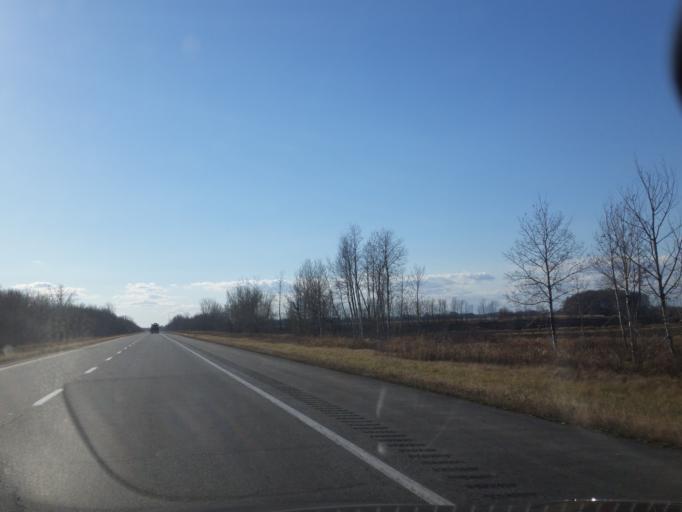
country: CA
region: Quebec
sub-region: Mauricie
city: Louiseville
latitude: 46.2510
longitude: -72.8885
